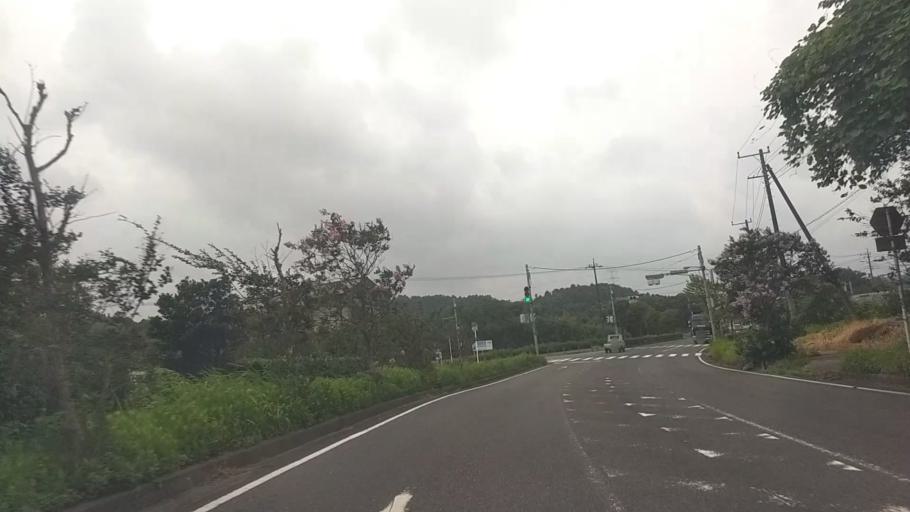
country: JP
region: Chiba
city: Kisarazu
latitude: 35.3752
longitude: 140.0126
